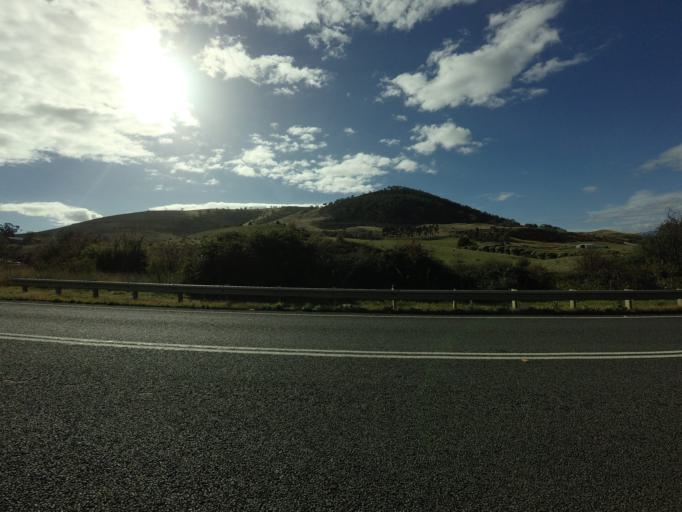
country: AU
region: Tasmania
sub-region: Derwent Valley
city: New Norfolk
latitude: -42.7201
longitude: 146.9482
